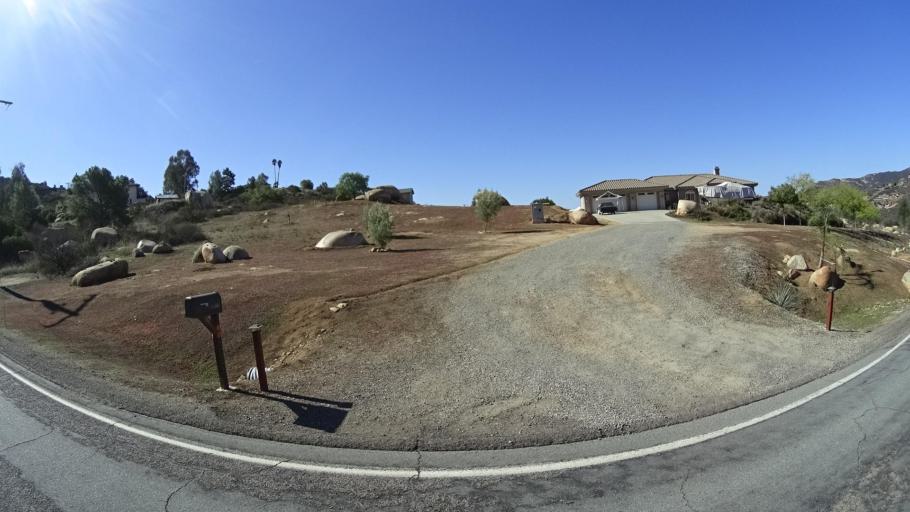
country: US
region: California
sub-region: San Diego County
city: Jamul
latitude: 32.7084
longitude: -116.7929
